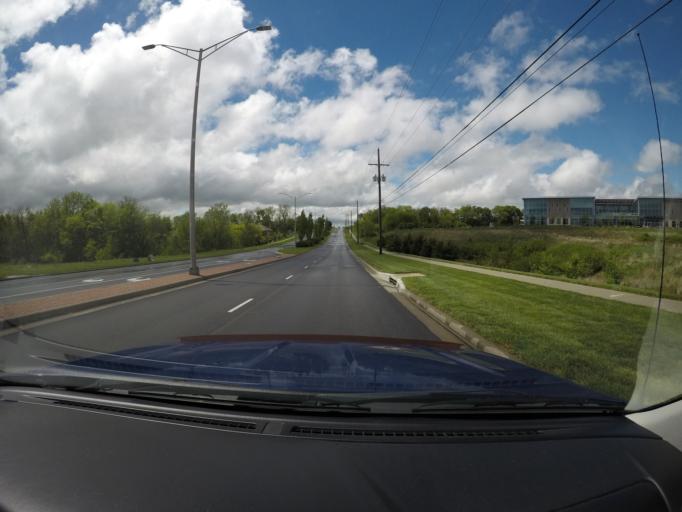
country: US
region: Kansas
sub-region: Johnson County
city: Olathe
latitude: 38.9274
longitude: -94.8412
